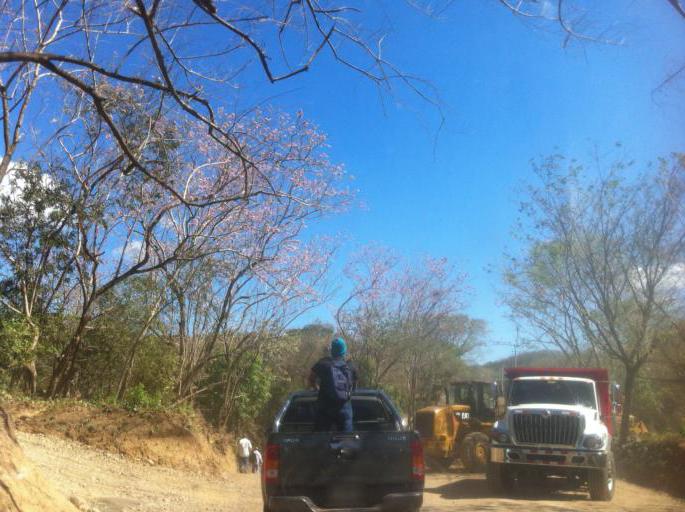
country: NI
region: Rivas
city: Tola
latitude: 11.3978
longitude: -85.9925
